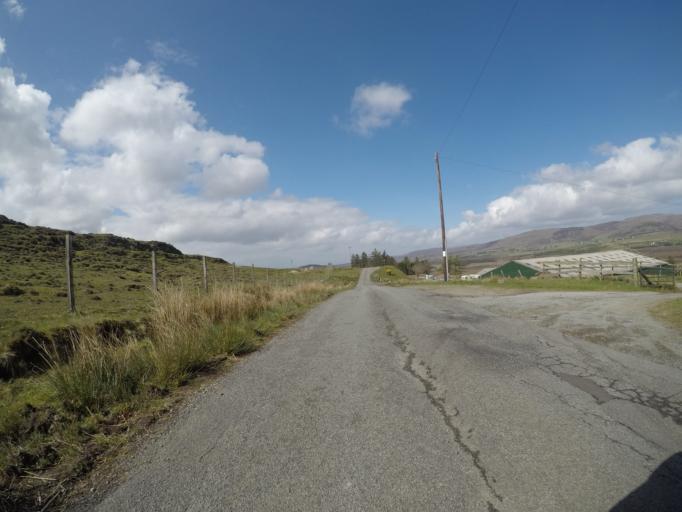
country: GB
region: Scotland
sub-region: Highland
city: Isle of Skye
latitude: 57.4249
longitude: -6.2687
